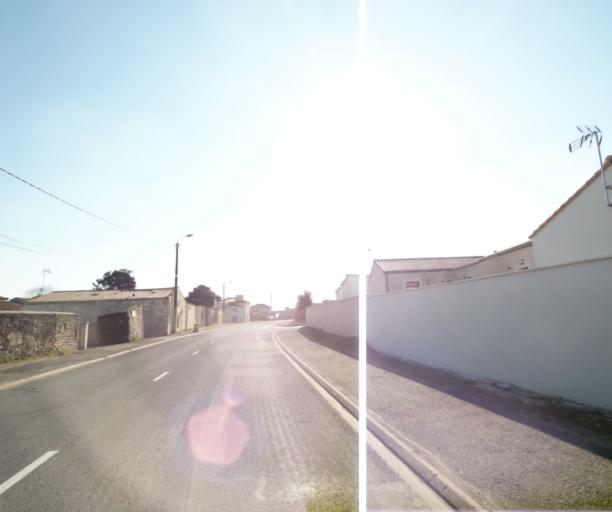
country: FR
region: Poitou-Charentes
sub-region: Departement des Deux-Sevres
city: Aiffres
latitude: 46.3220
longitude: -0.4207
